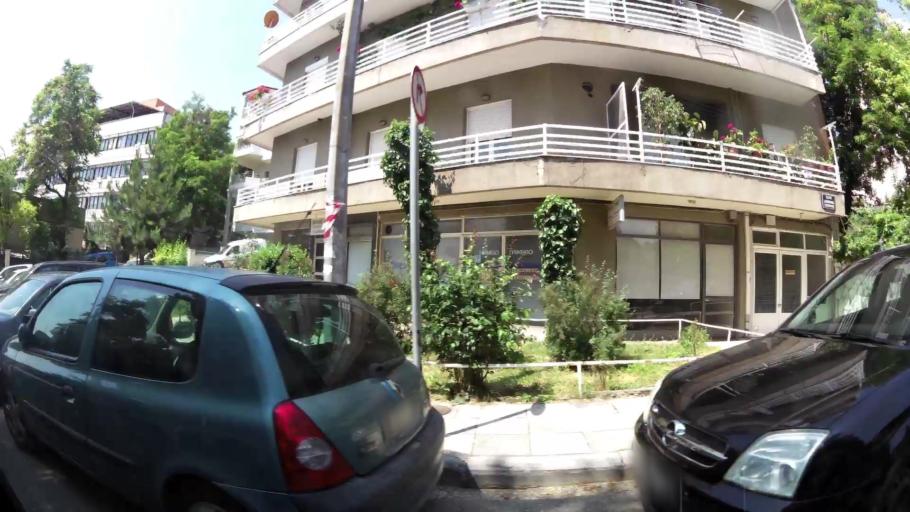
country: GR
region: West Macedonia
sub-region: Nomos Kozanis
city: Kozani
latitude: 40.3056
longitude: 21.7839
